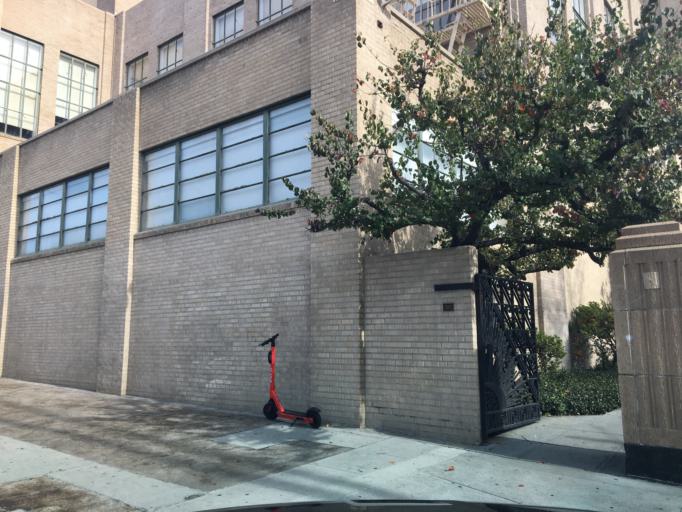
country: US
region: California
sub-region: Los Angeles County
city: Silver Lake
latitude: 34.0612
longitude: -118.2891
